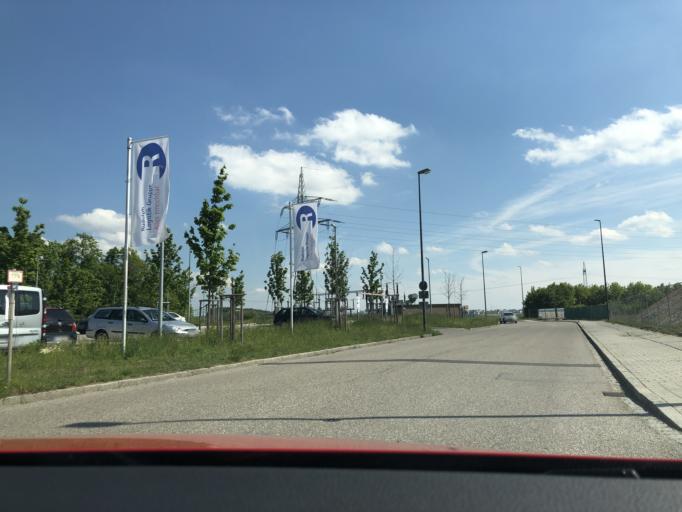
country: DE
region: Bavaria
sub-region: Upper Bavaria
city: Grossmehring
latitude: 48.7891
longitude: 11.5138
